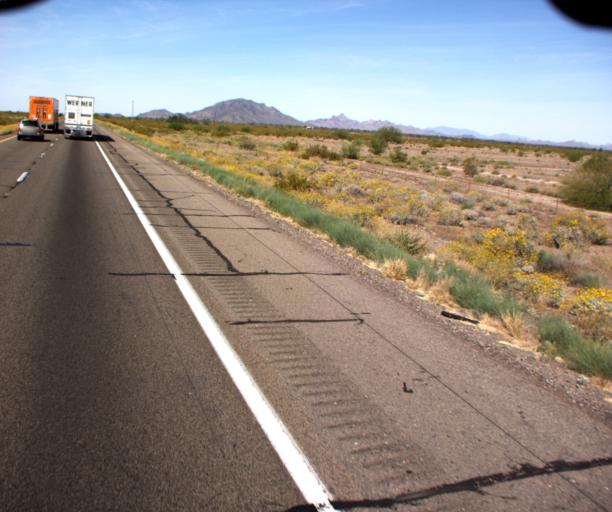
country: US
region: Arizona
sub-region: Maricopa County
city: Buckeye
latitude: 33.5035
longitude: -112.9672
